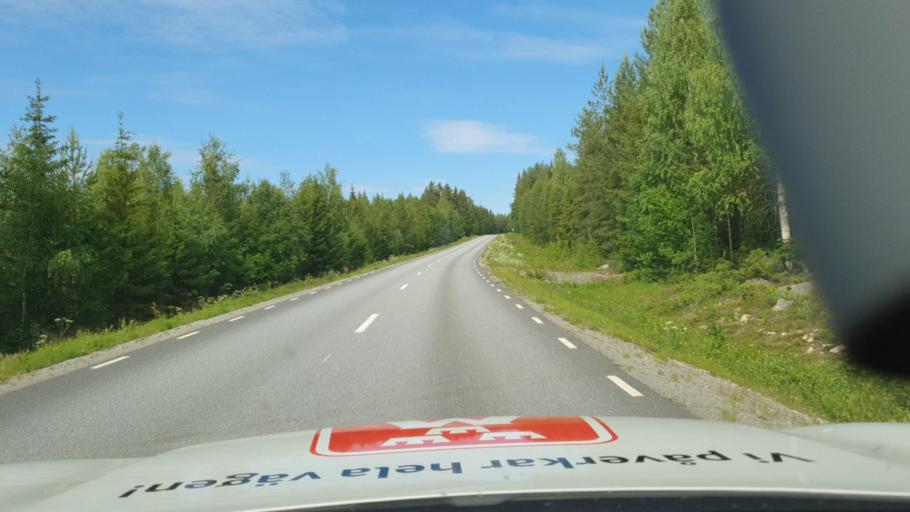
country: SE
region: Vaesterbotten
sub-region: Skelleftea Kommun
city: Forsbacka
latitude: 64.7098
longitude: 20.4289
